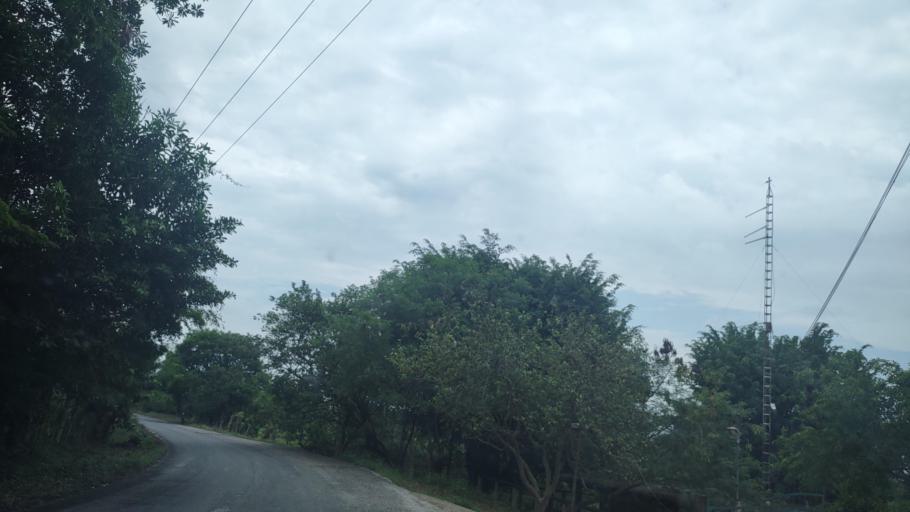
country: MX
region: Tabasco
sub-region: Huimanguillo
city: Francisco Rueda
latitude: 17.5246
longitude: -94.1246
